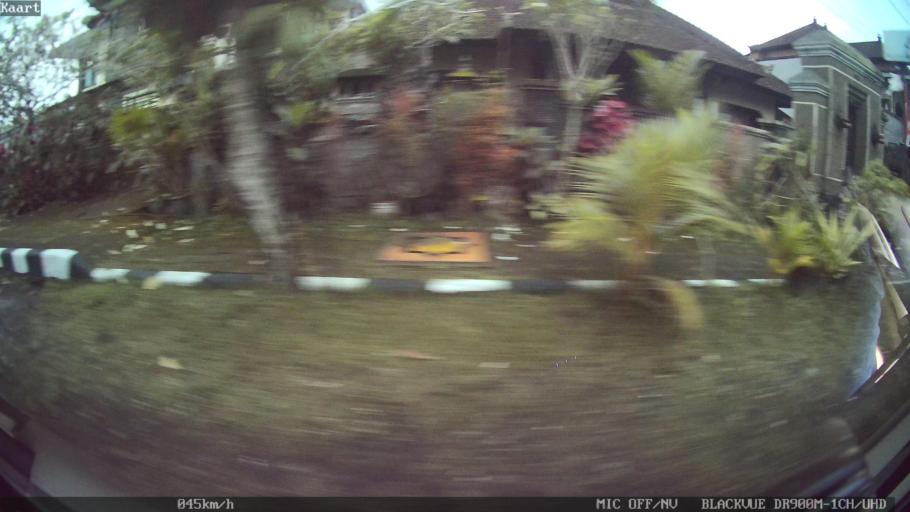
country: ID
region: Bali
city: Pohgending Kawan
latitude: -8.4366
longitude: 115.1427
